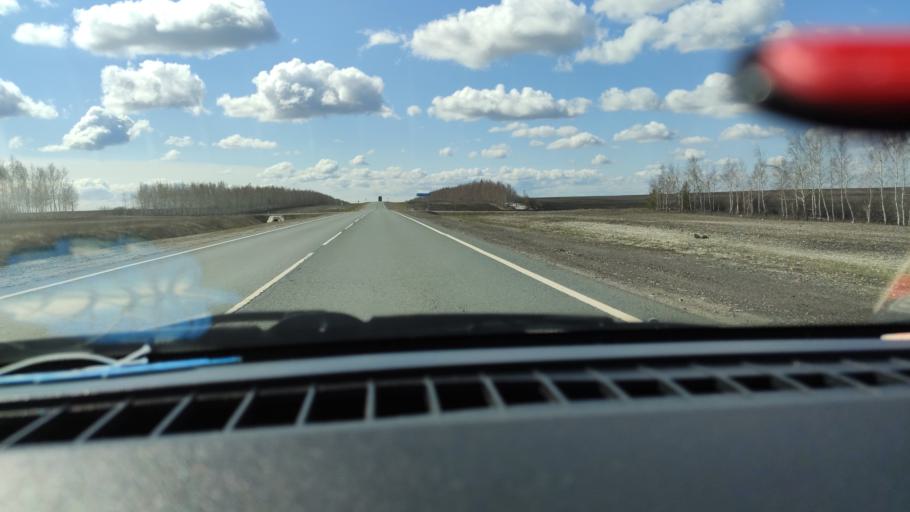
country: RU
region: Samara
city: Syzran'
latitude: 52.9102
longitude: 48.2993
